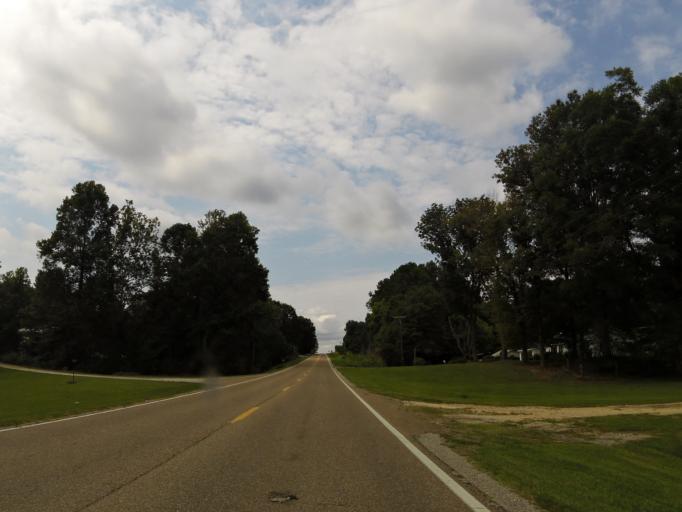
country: US
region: Tennessee
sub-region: Henderson County
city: Lexington
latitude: 35.5102
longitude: -88.3168
